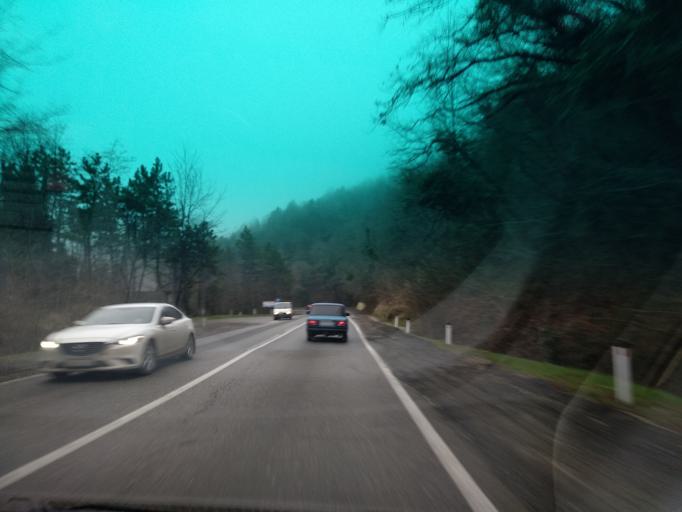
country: RU
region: Krasnodarskiy
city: Agoy
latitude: 44.1378
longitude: 39.0534
